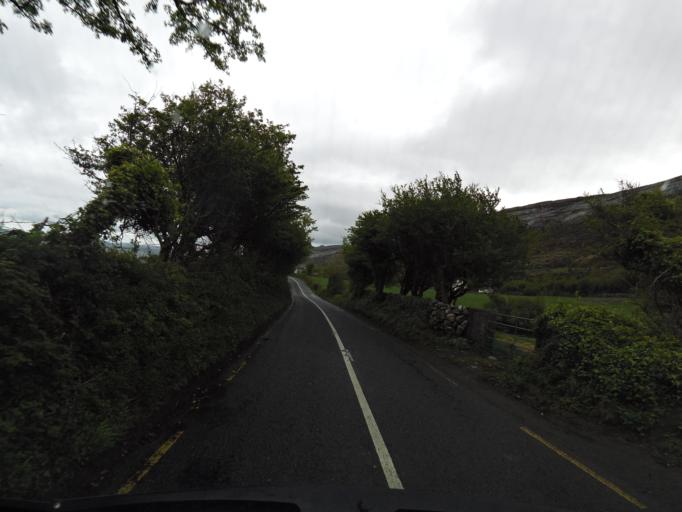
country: IE
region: Connaught
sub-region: County Galway
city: Bearna
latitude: 53.1414
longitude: -9.2291
